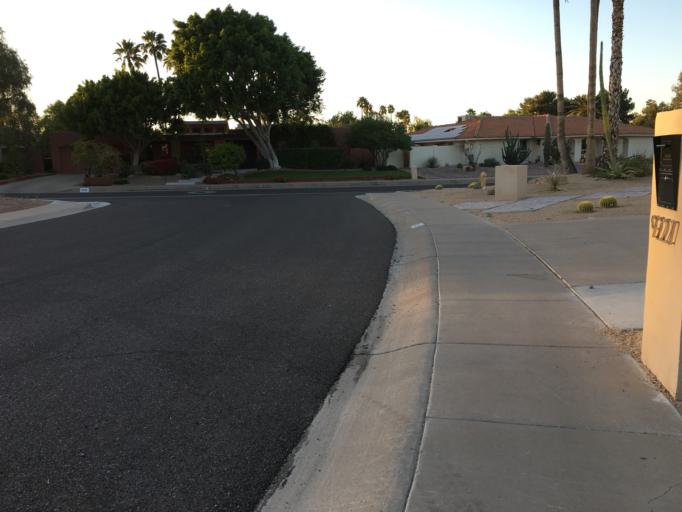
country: US
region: Arizona
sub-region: Maricopa County
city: Paradise Valley
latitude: 33.5708
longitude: -112.0091
